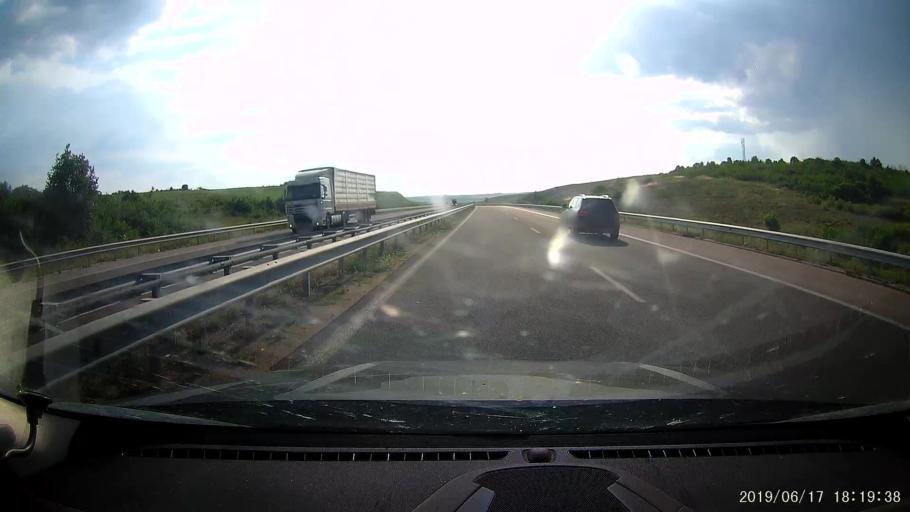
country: BG
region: Khaskovo
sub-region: Obshtina Kharmanli
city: Kharmanli
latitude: 41.9629
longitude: 25.8403
